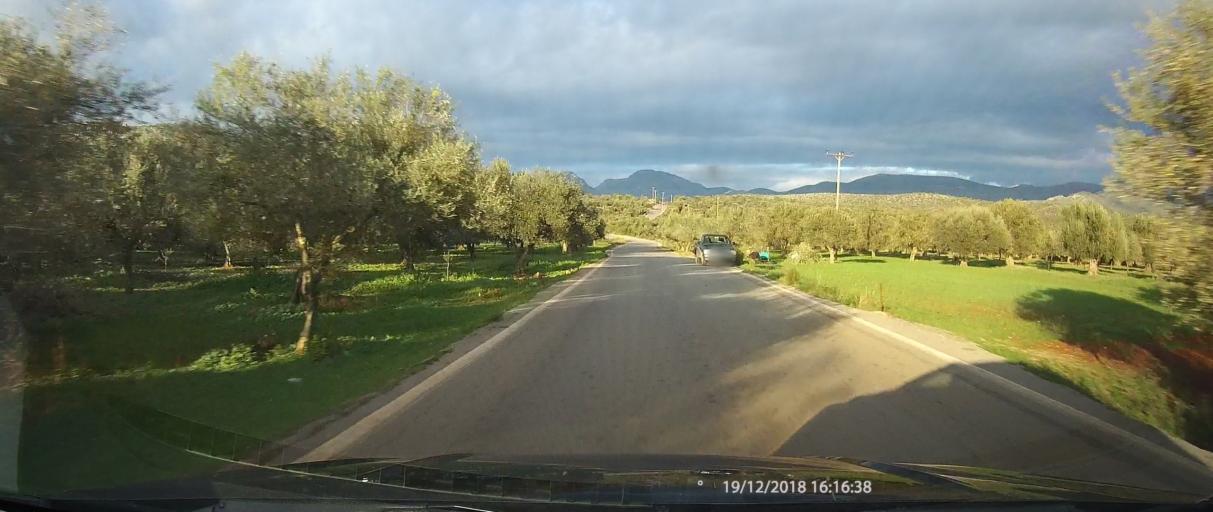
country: GR
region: Peloponnese
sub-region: Nomos Lakonias
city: Kato Glikovrisi
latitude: 36.9023
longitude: 22.8051
